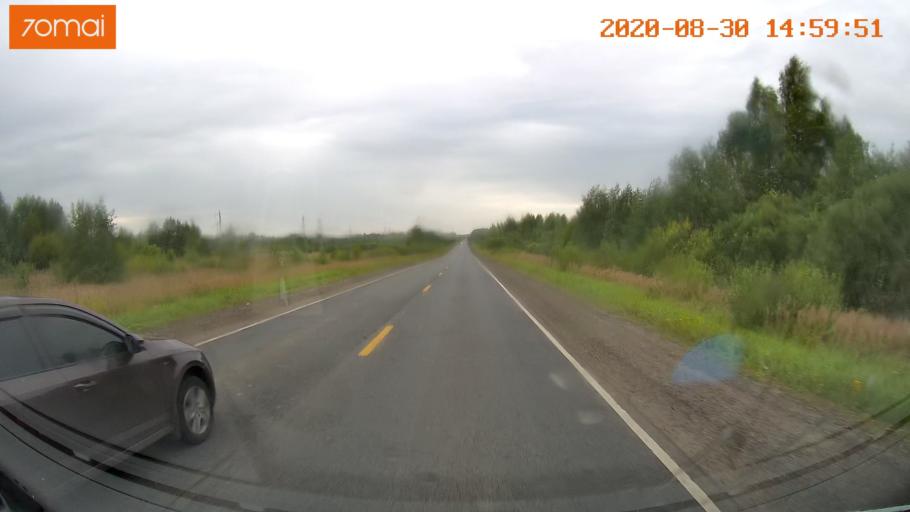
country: RU
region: Ivanovo
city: Staraya Vichuga
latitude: 57.3372
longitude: 41.9667
